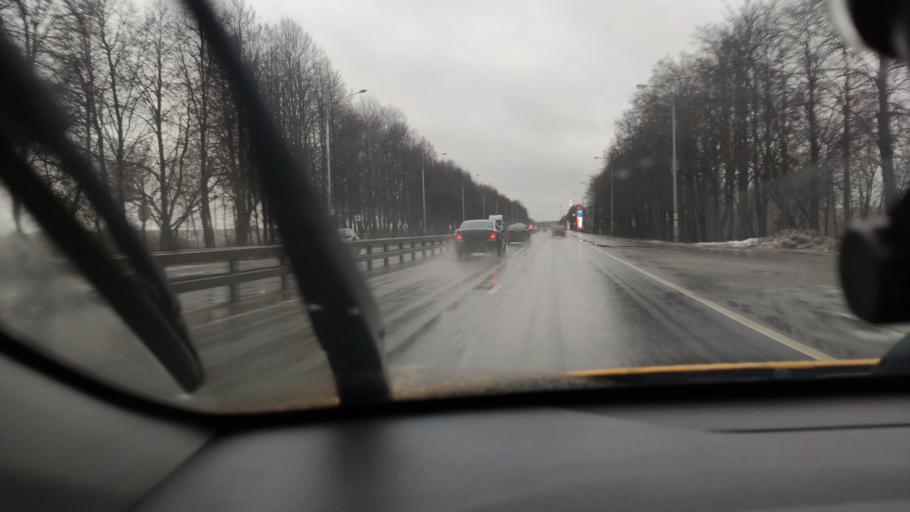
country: RU
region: Moskovskaya
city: Dubrovitsy
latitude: 55.3933
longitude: 37.4311
